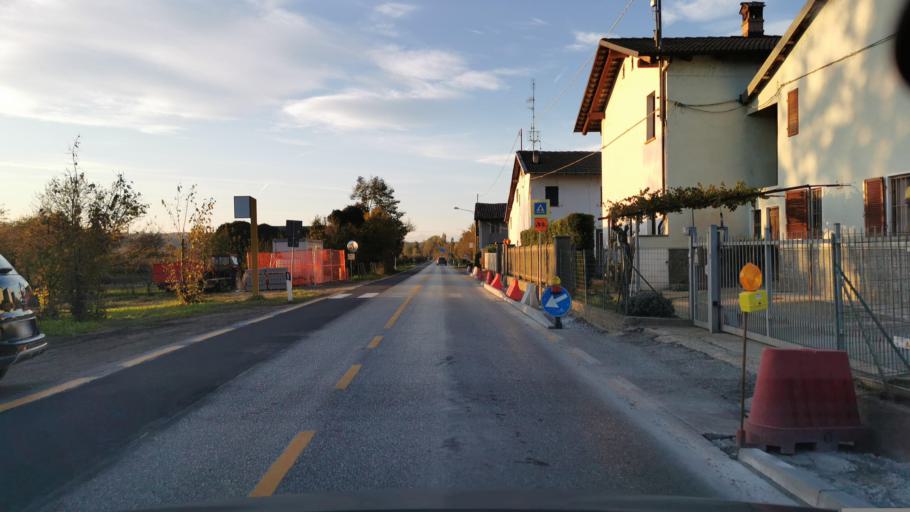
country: IT
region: Piedmont
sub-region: Provincia di Cuneo
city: Monchiero Borgonuovo
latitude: 44.5777
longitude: 7.9134
